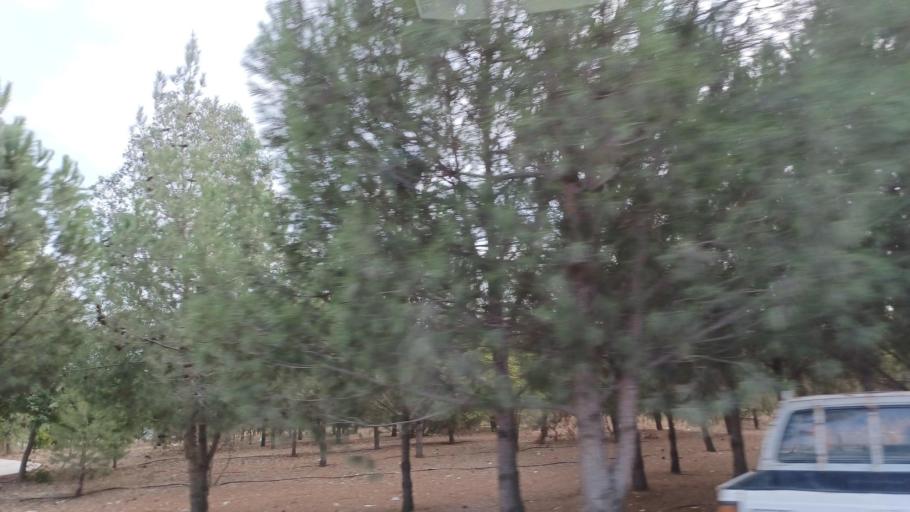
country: CY
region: Lefkosia
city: Peristerona
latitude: 35.1287
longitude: 33.0831
